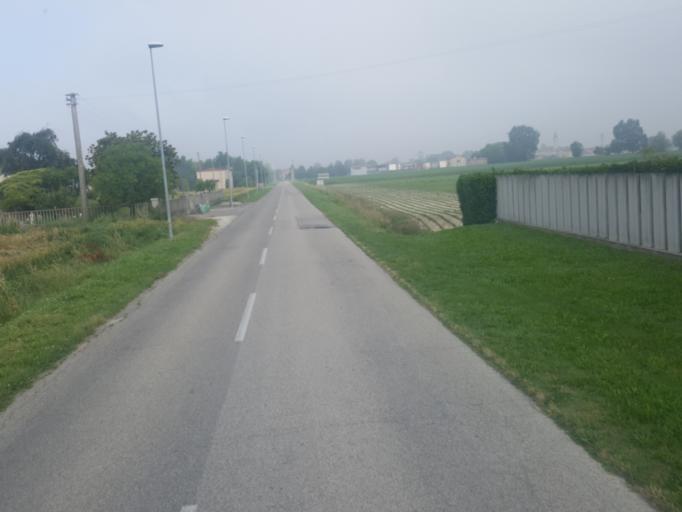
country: IT
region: Veneto
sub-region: Provincia di Rovigo
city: Canaro
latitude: 44.9289
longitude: 11.6834
